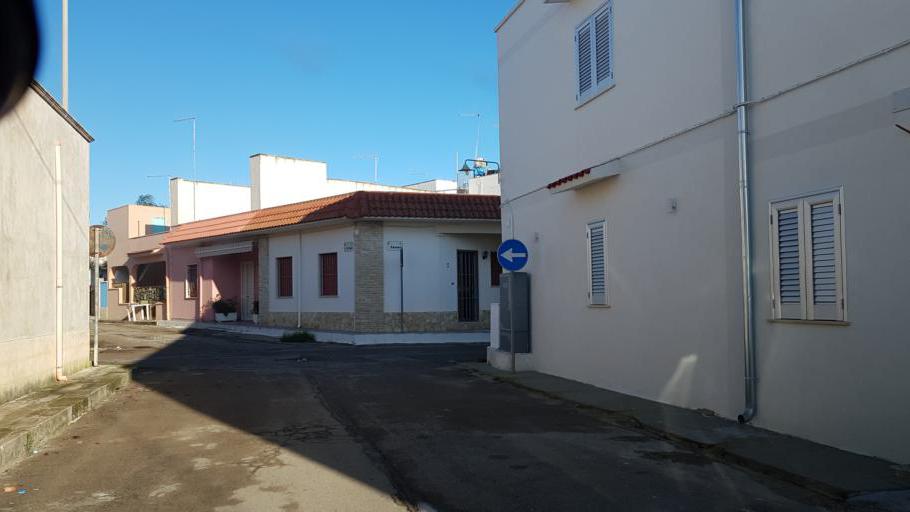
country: IT
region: Apulia
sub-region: Provincia di Brindisi
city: Torchiarolo
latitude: 40.5351
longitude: 18.0740
